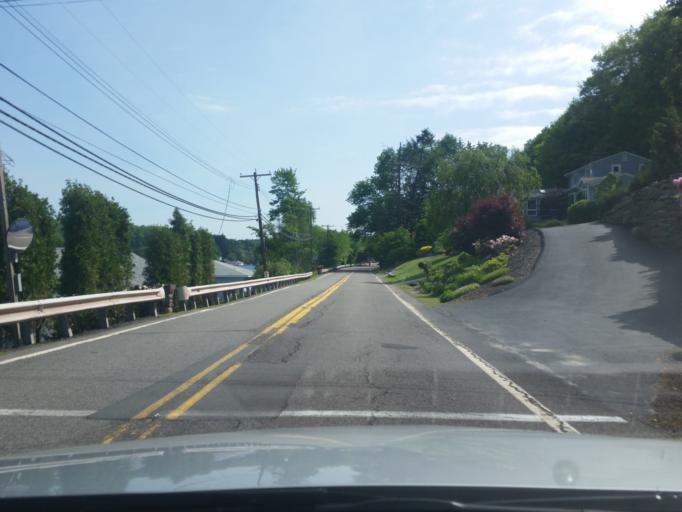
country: US
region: Pennsylvania
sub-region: Luzerne County
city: Harveys Lake
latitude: 41.3716
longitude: -76.0384
